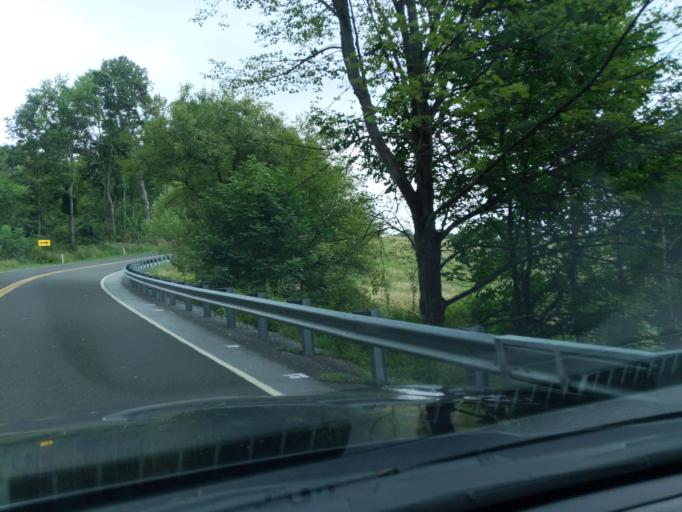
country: US
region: Pennsylvania
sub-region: Blair County
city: Claysburg
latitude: 40.3555
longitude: -78.5078
